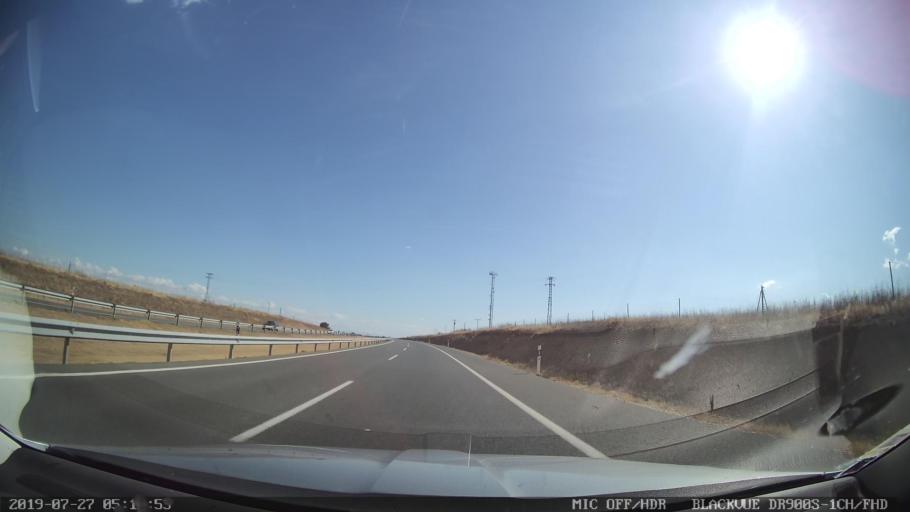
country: ES
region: Castille-La Mancha
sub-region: Province of Toledo
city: Quismondo
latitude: 40.1085
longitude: -4.3319
